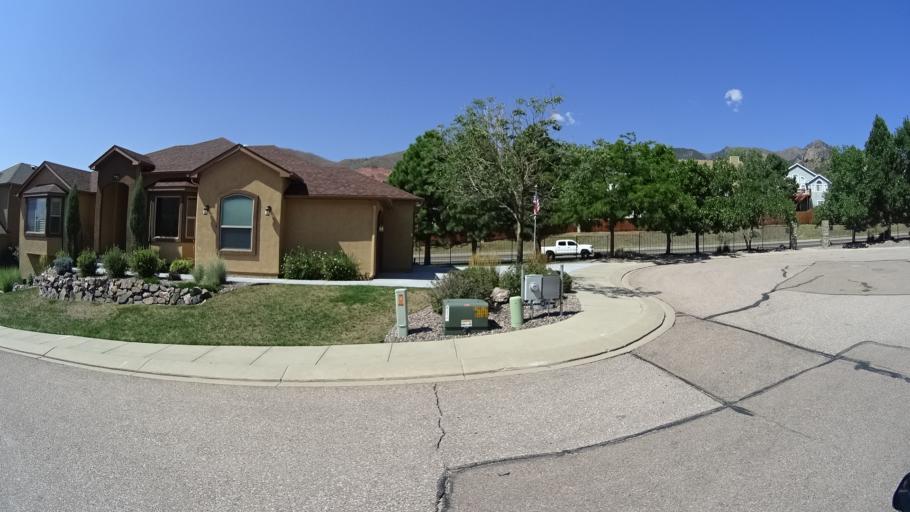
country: US
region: Colorado
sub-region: El Paso County
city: Air Force Academy
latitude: 38.9394
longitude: -104.8756
